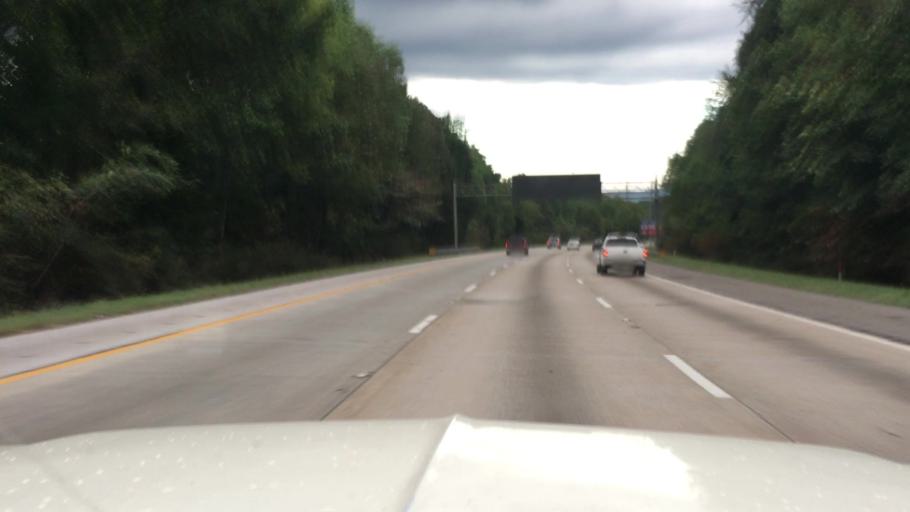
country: US
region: Alabama
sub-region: Jefferson County
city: Hoover
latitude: 33.4251
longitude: -86.8176
